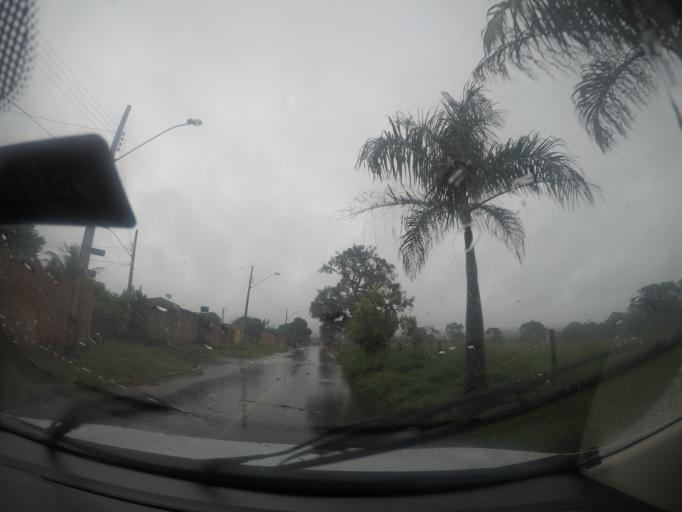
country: BR
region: Goias
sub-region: Goianira
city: Goianira
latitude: -16.5909
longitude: -49.3482
